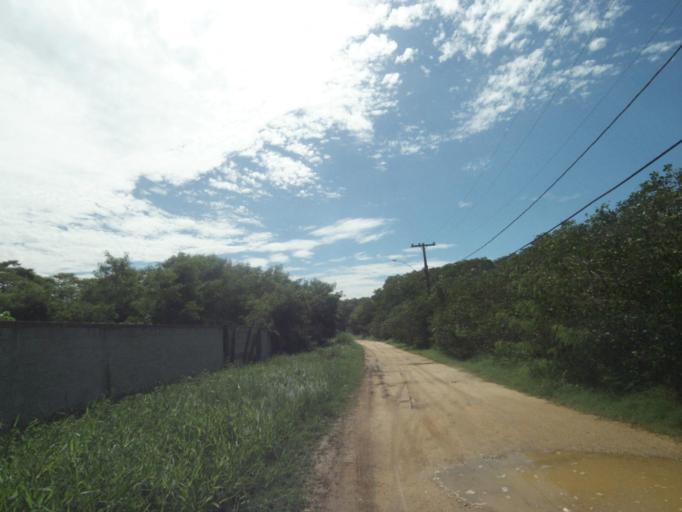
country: BR
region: Rio de Janeiro
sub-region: Niteroi
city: Niteroi
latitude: -22.9510
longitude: -43.0458
